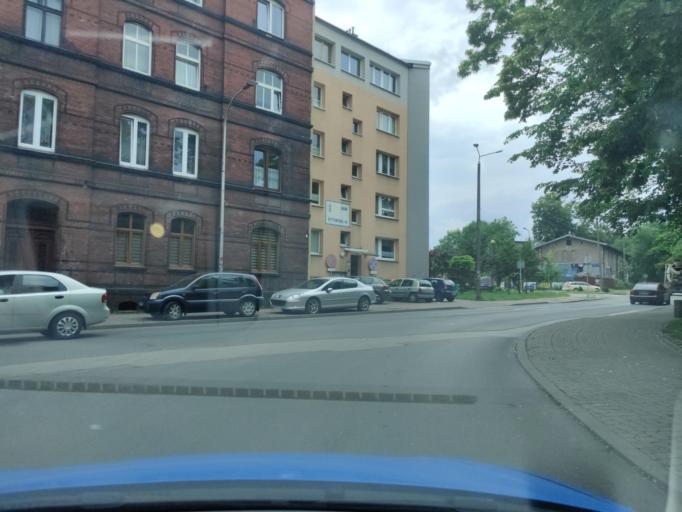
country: PL
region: Silesian Voivodeship
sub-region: Sosnowiec
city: Sosnowiec
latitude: 50.2475
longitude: 19.1328
